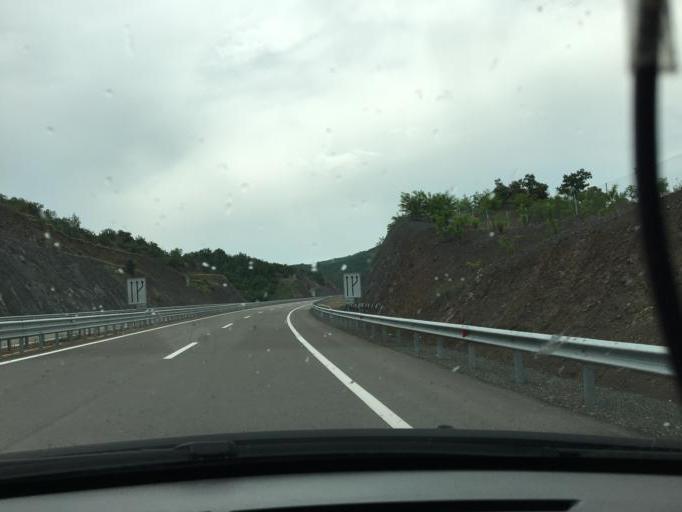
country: MK
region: Demir Kapija
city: Demir Kapija
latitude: 41.3684
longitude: 22.3418
